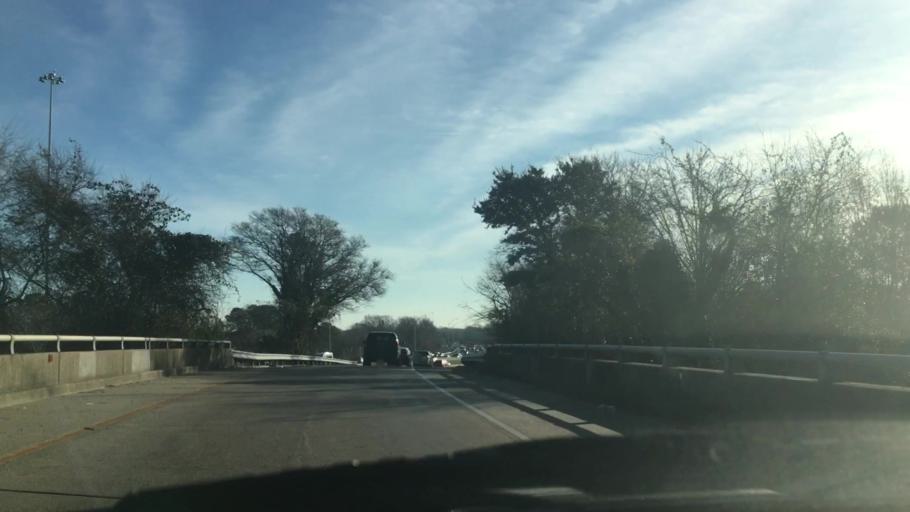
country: US
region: Virginia
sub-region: City of Norfolk
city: Norfolk
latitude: 36.9042
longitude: -76.2544
